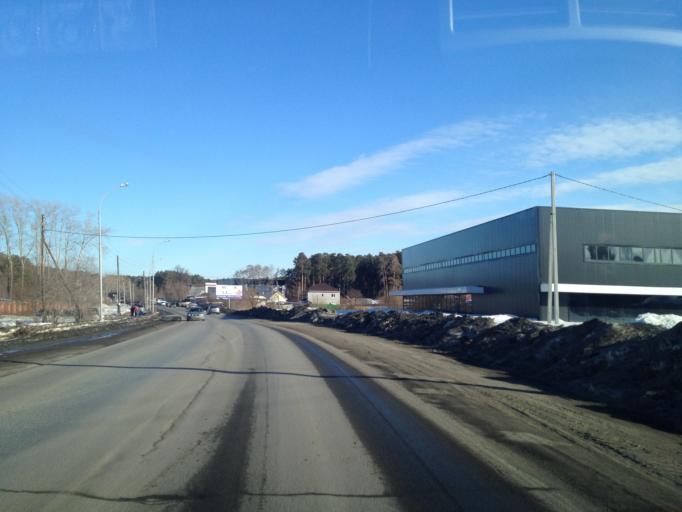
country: RU
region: Sverdlovsk
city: Shirokaya Rechka
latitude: 56.8175
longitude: 60.5136
